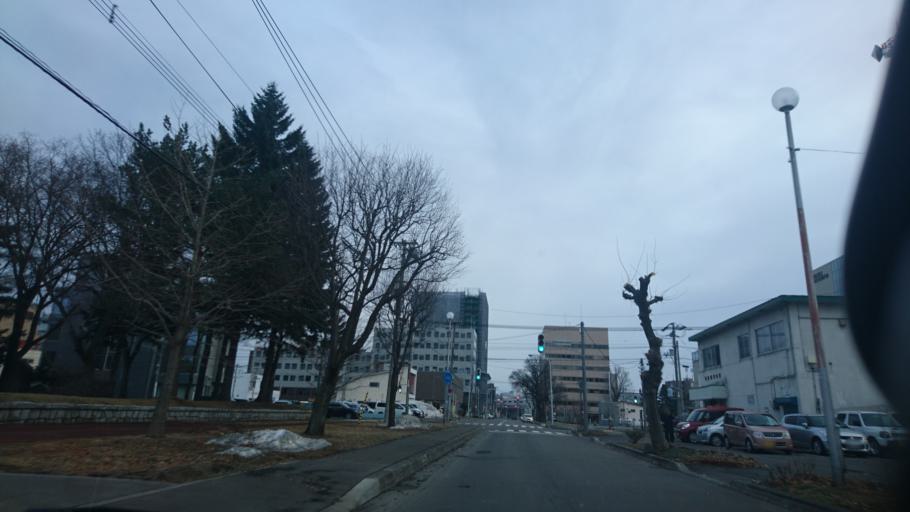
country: JP
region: Hokkaido
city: Obihiro
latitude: 42.9240
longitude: 143.1987
